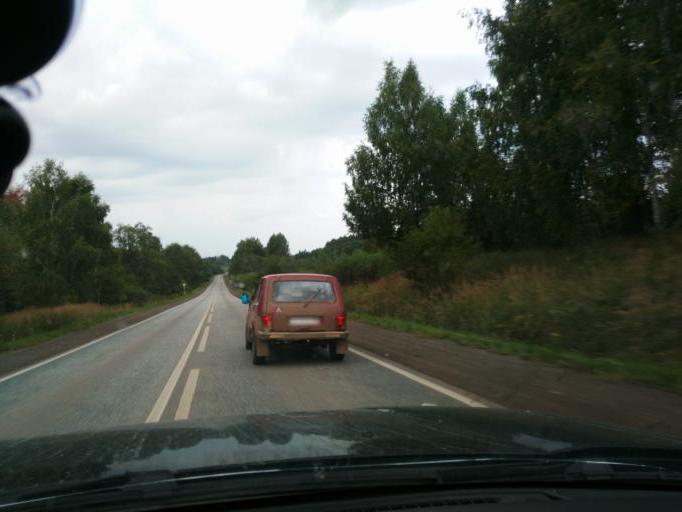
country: RU
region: Perm
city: Chernushka
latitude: 56.8393
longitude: 55.9932
